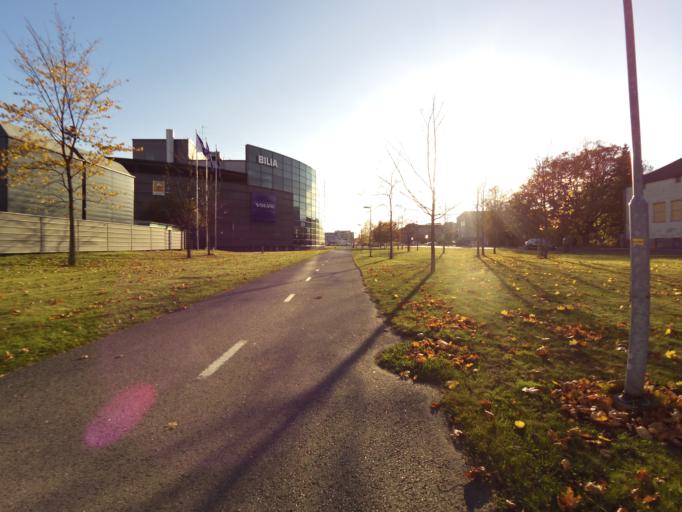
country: FI
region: Uusimaa
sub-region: Helsinki
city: Vantaa
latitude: 60.1965
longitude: 25.0397
